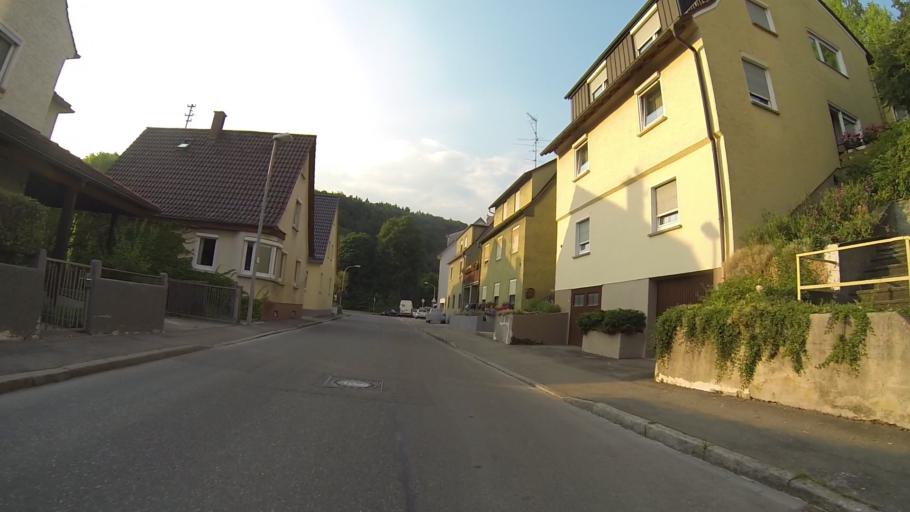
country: DE
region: Baden-Wuerttemberg
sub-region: Tuebingen Region
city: Dornstadt
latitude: 48.4205
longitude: 9.9189
